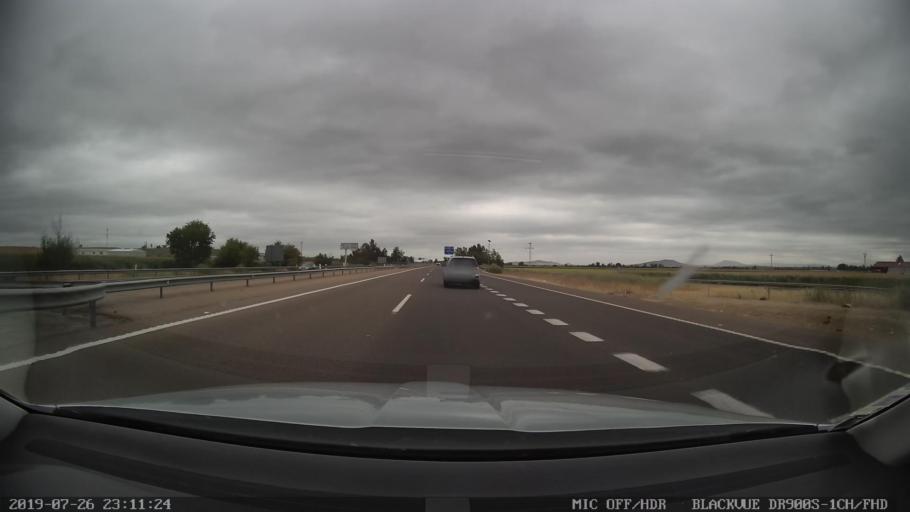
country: ES
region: Extremadura
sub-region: Provincia de Badajoz
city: Valdetorres
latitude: 38.9907
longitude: -6.1098
